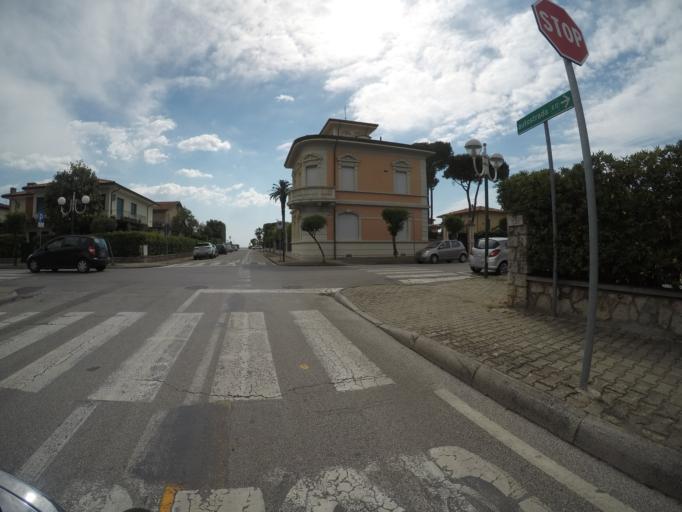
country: IT
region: Tuscany
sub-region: Provincia di Lucca
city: Forte dei Marmi
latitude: 43.9614
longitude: 10.1652
